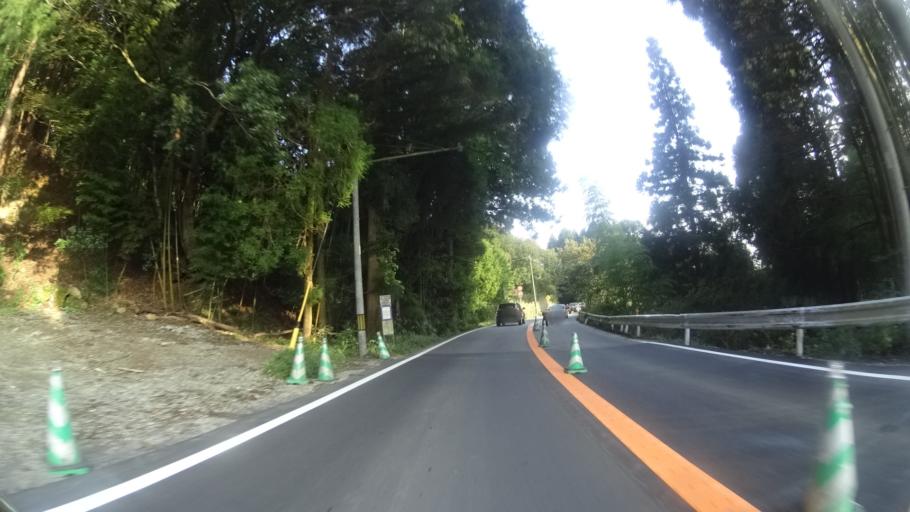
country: JP
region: Oita
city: Beppu
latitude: 33.2700
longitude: 131.4354
